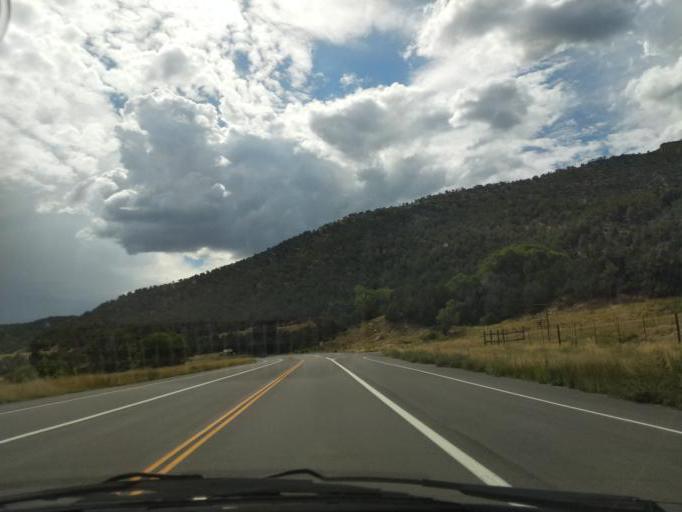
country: US
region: Colorado
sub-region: Delta County
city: Paonia
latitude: 38.9125
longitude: -107.5537
